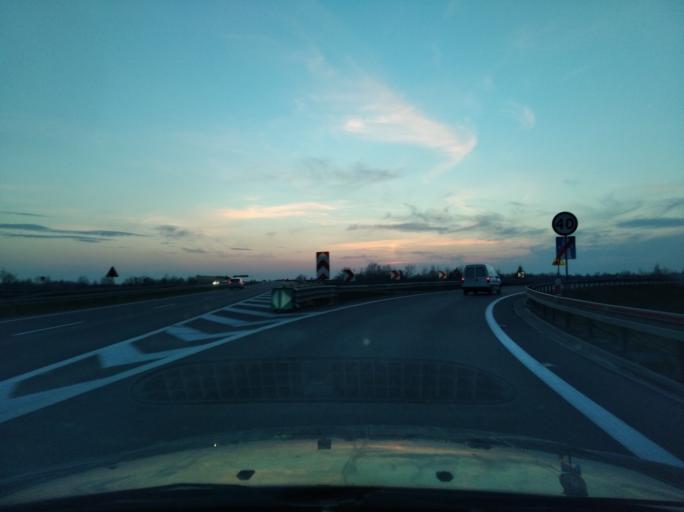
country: PL
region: Subcarpathian Voivodeship
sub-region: Powiat rzeszowski
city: Rudna Mala
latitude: 50.1084
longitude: 21.9811
